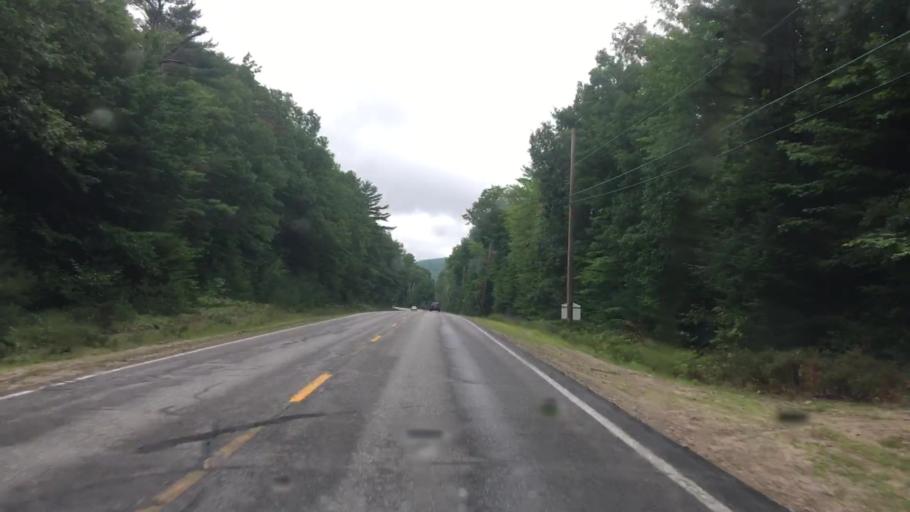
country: US
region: Maine
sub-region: Oxford County
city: Fryeburg
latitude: 43.9929
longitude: -70.9376
